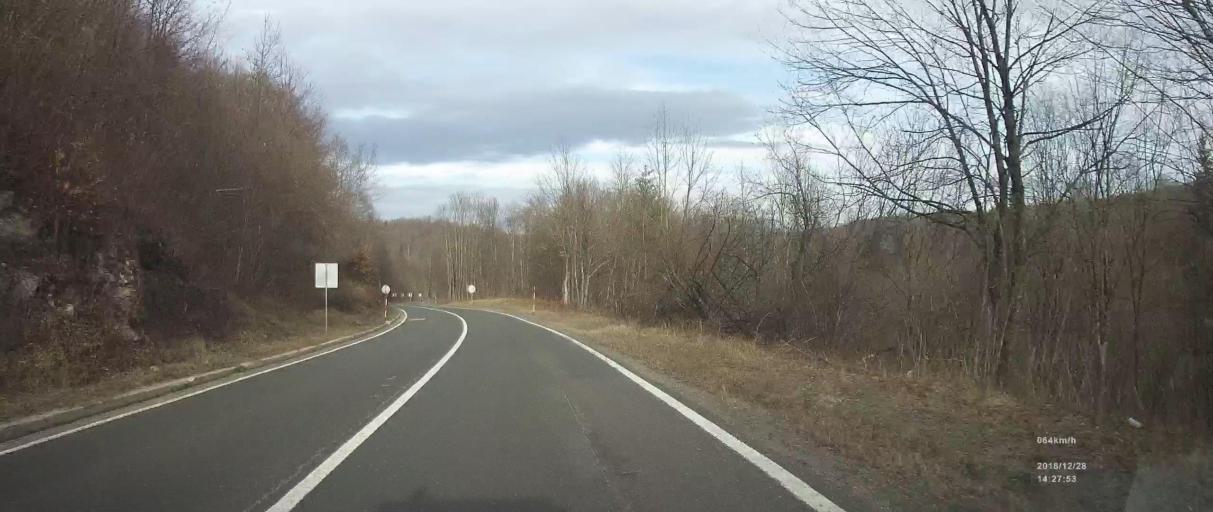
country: HR
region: Primorsko-Goranska
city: Vrbovsko
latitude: 45.4055
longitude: 15.1094
